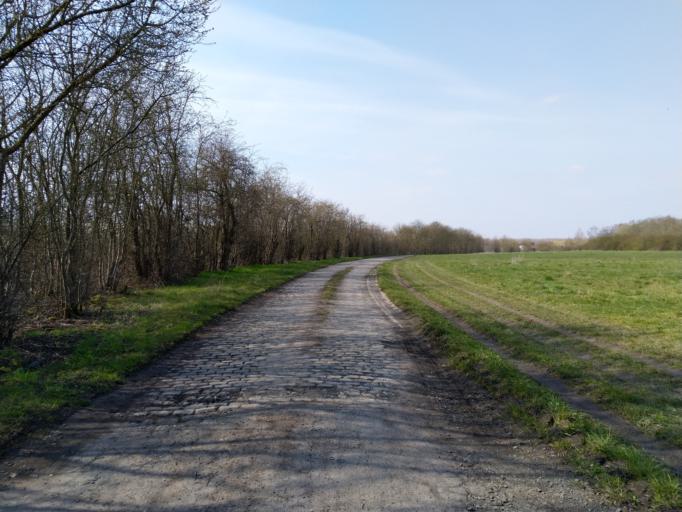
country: BE
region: Wallonia
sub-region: Province du Hainaut
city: Chasse Royale
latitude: 50.4305
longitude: 3.9376
